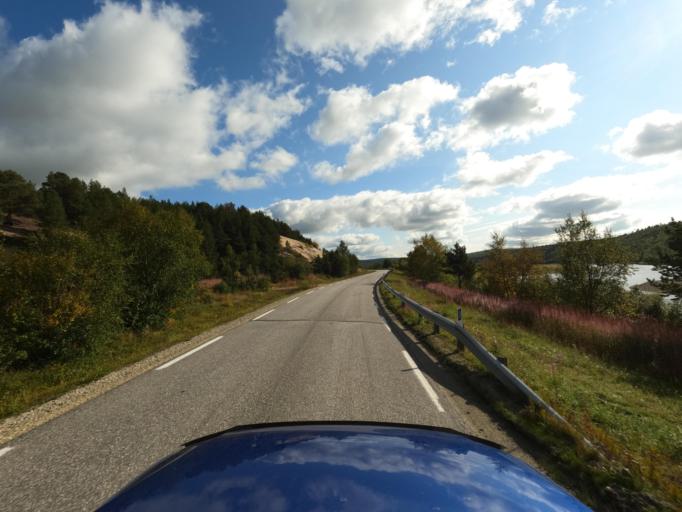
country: NO
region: Finnmark Fylke
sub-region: Karasjok
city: Karasjohka
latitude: 69.4447
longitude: 25.2124
